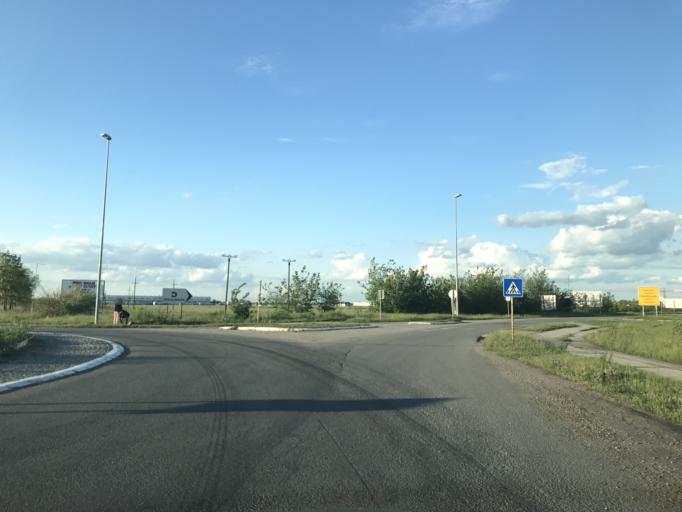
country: RS
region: Autonomna Pokrajina Vojvodina
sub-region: Srednjebanatski Okrug
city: Zrenjanin
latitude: 45.3806
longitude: 20.3515
